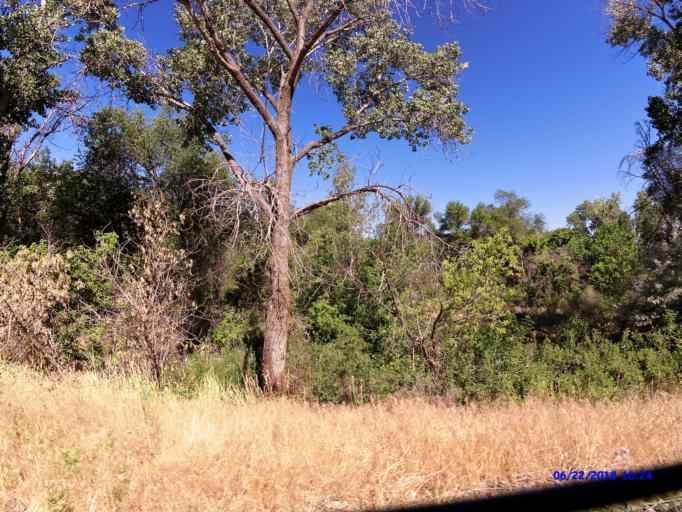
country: US
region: Utah
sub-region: Weber County
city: South Ogden
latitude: 41.2050
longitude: -111.9889
